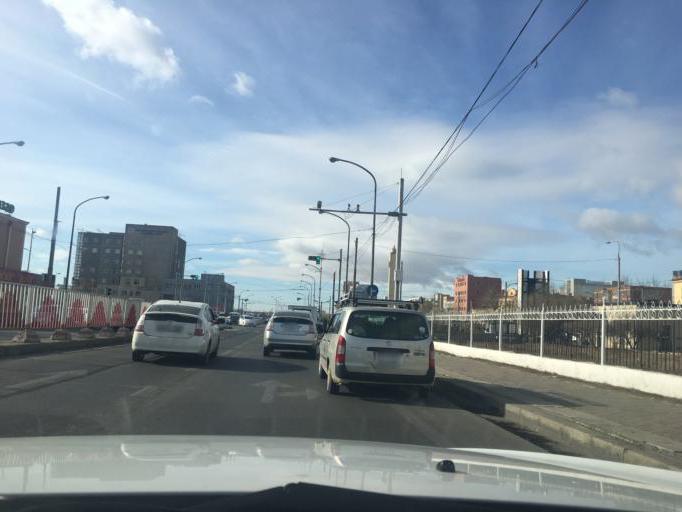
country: MN
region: Ulaanbaatar
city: Ulaanbaatar
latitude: 47.9092
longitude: 106.8856
